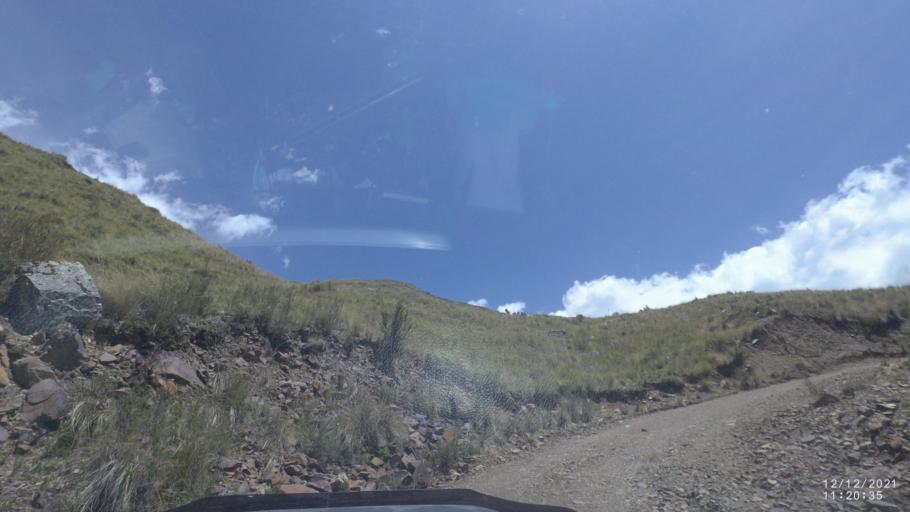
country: BO
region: Cochabamba
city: Cochabamba
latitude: -17.3015
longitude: -66.1843
